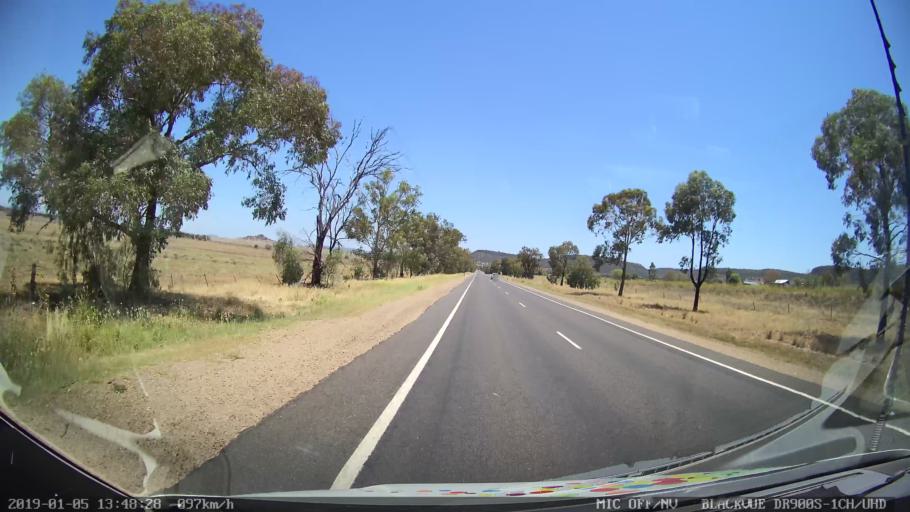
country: AU
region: New South Wales
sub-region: Gunnedah
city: Gunnedah
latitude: -31.0023
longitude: 150.2779
